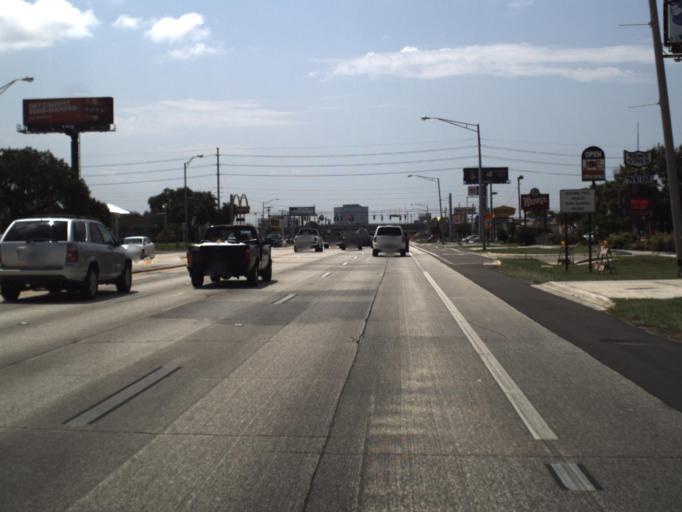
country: US
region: Florida
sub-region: Hillsborough County
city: Tampa
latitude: 27.9615
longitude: -82.5057
